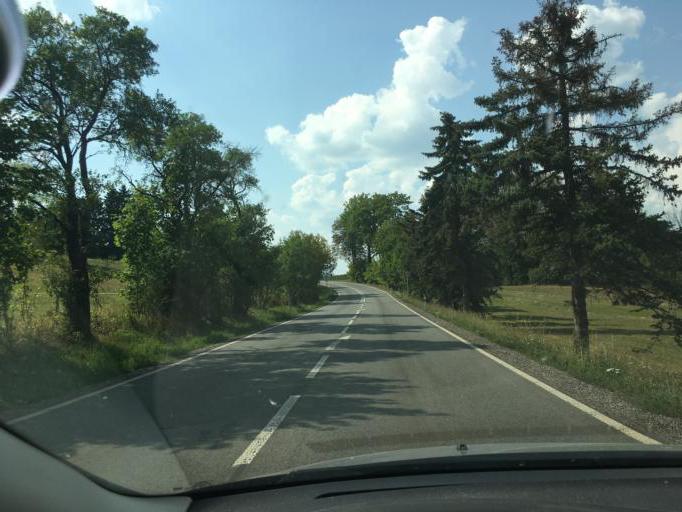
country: CZ
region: Kralovehradecky
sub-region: Okres Trutnov
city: Rudnik
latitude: 50.6135
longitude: 15.6871
